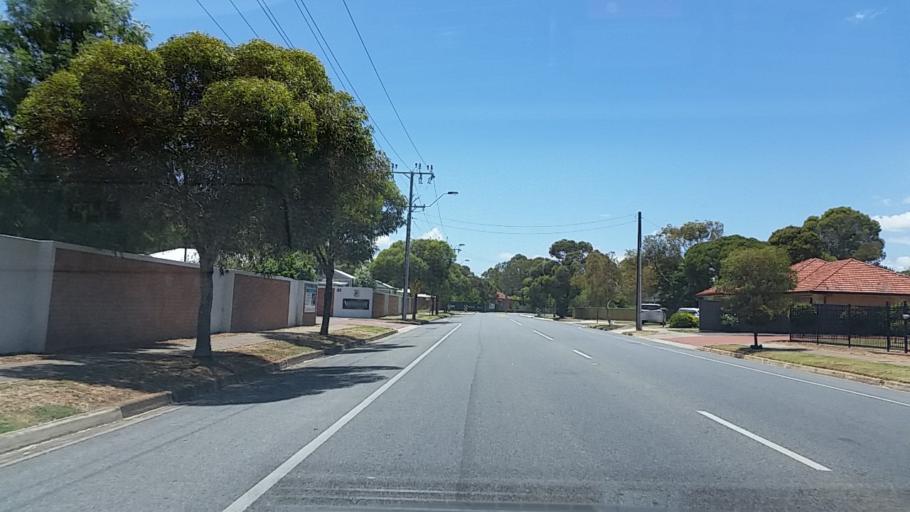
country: AU
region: South Australia
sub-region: Salisbury
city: Salisbury
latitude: -34.7638
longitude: 138.6291
